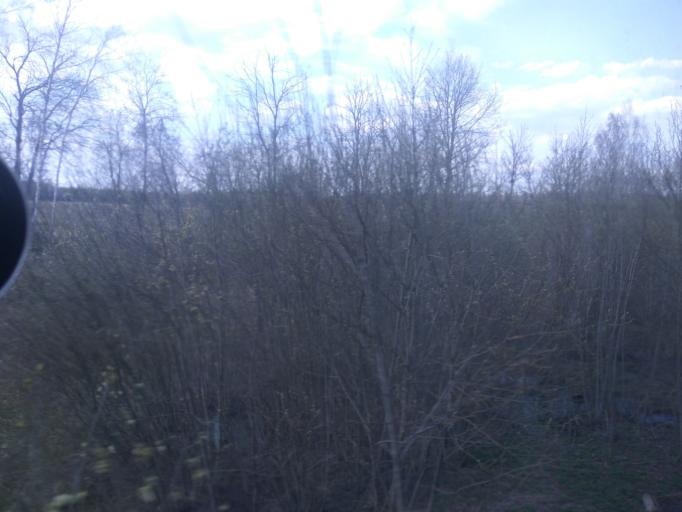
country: RU
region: Moskovskaya
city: Budenovetc
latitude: 56.3109
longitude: 37.6528
